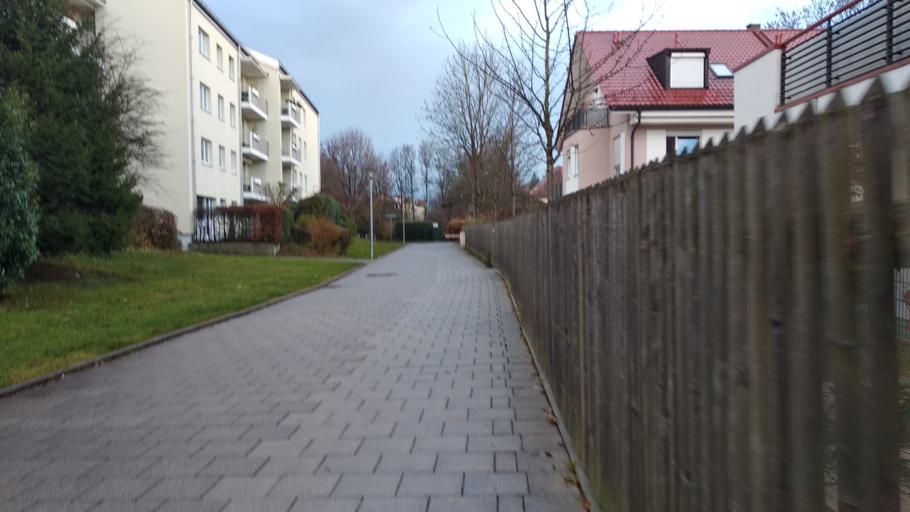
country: DE
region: Bavaria
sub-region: Upper Bavaria
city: Neubiberg
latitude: 48.1024
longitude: 11.6330
